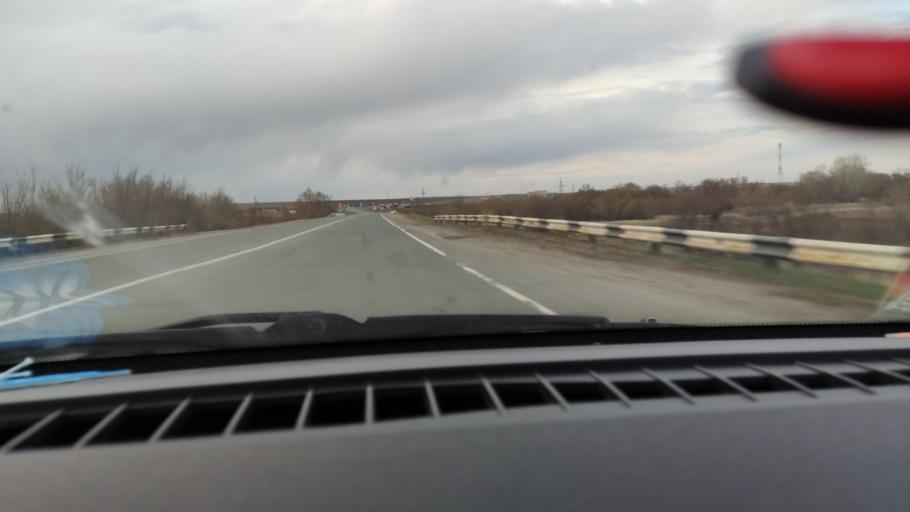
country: RU
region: Saratov
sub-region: Saratovskiy Rayon
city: Saratov
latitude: 51.7294
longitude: 46.0322
